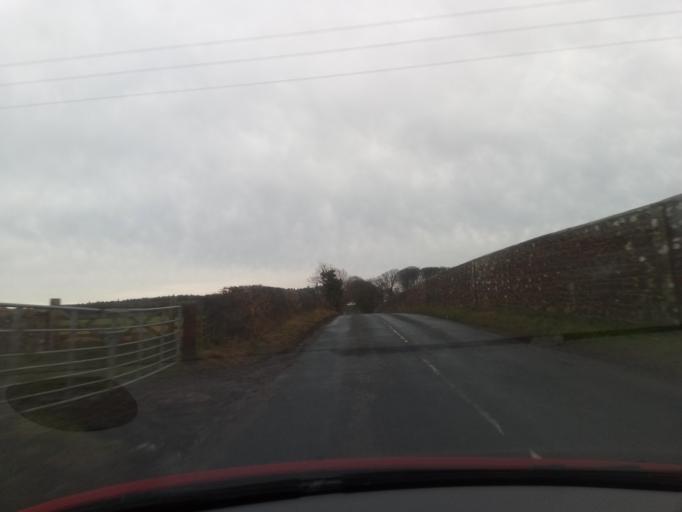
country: GB
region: England
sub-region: Northumberland
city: Alnwick
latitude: 55.4439
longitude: -1.7343
